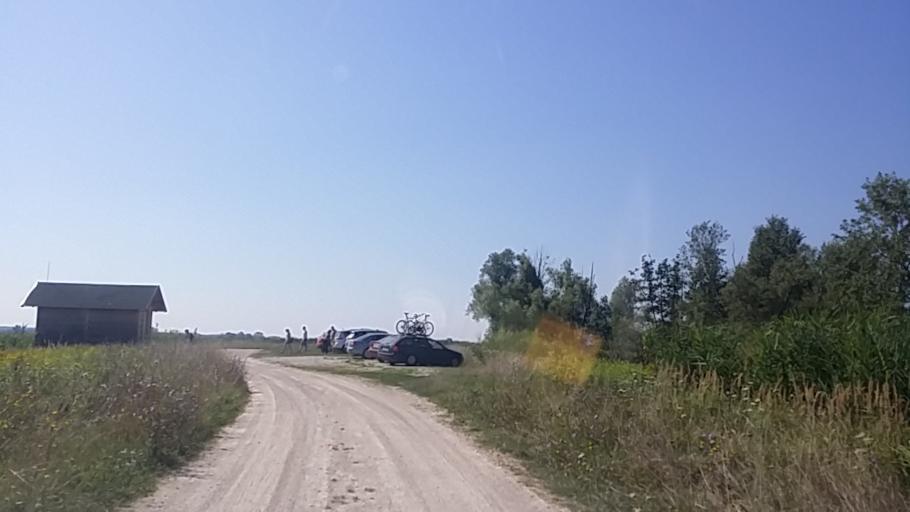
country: HU
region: Zala
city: Sarmellek
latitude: 46.6811
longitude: 17.2368
